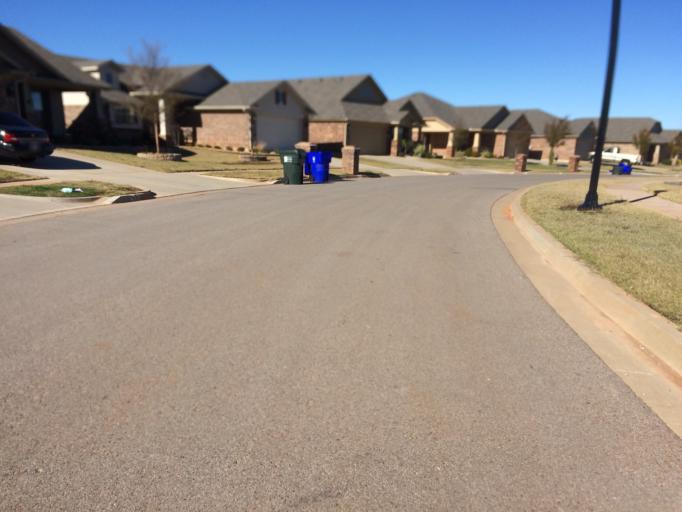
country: US
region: Oklahoma
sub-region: Cleveland County
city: Norman
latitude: 35.2599
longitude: -97.4577
